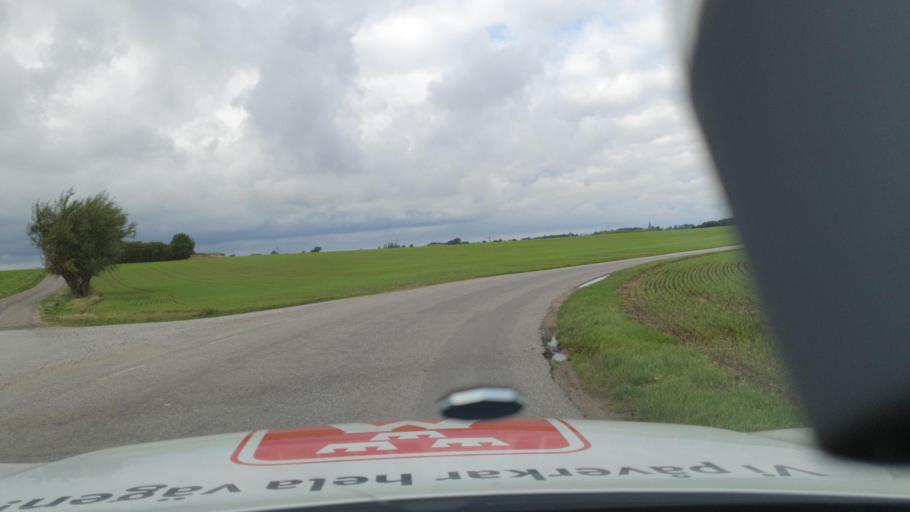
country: SE
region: Skane
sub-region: Trelleborgs Kommun
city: Skare
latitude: 55.4256
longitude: 13.0794
